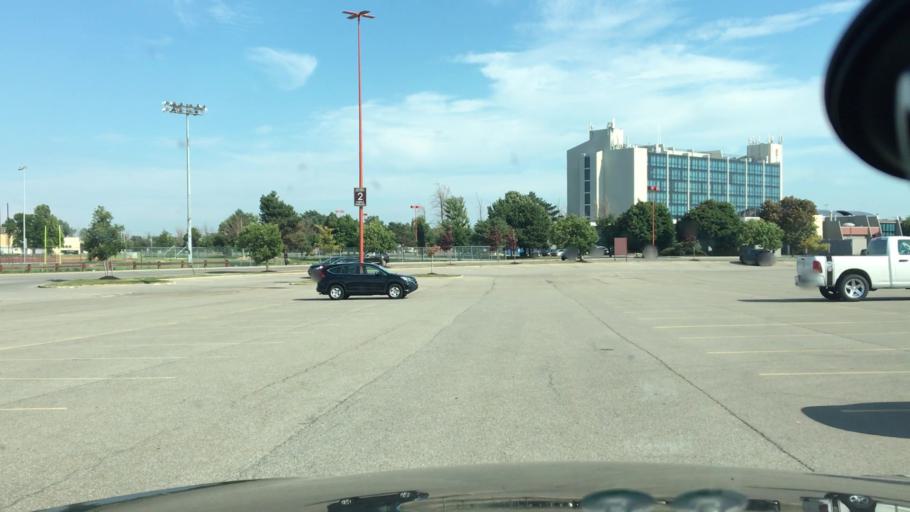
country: US
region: New York
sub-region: Erie County
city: Cheektowaga
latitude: 42.9114
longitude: -78.7617
